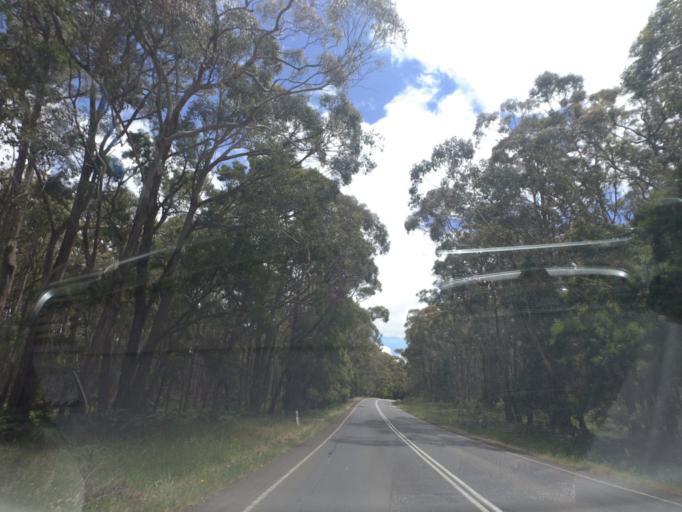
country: AU
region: Victoria
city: Brown Hill
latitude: -37.5047
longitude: 144.1589
